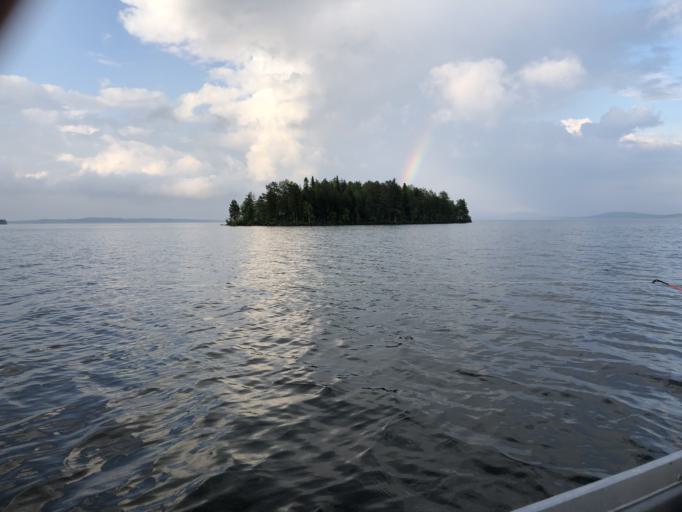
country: FI
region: Lapland
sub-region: Itae-Lappi
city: Posio
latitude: 66.1263
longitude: 28.5249
